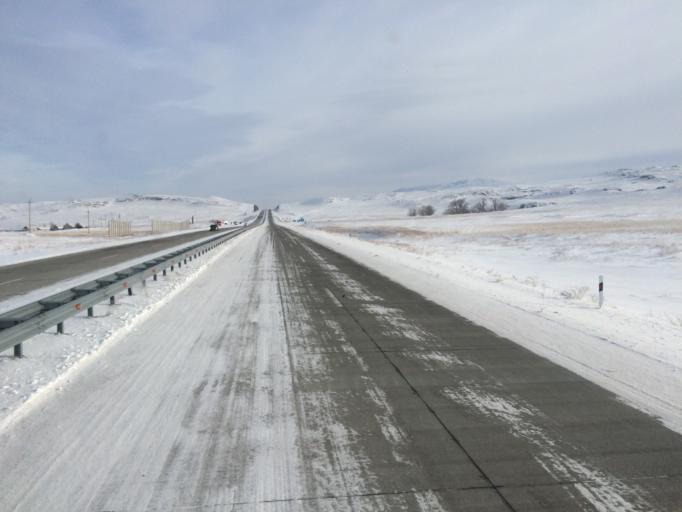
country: KZ
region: Zhambyl
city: Georgiyevka
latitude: 43.4339
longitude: 74.9297
